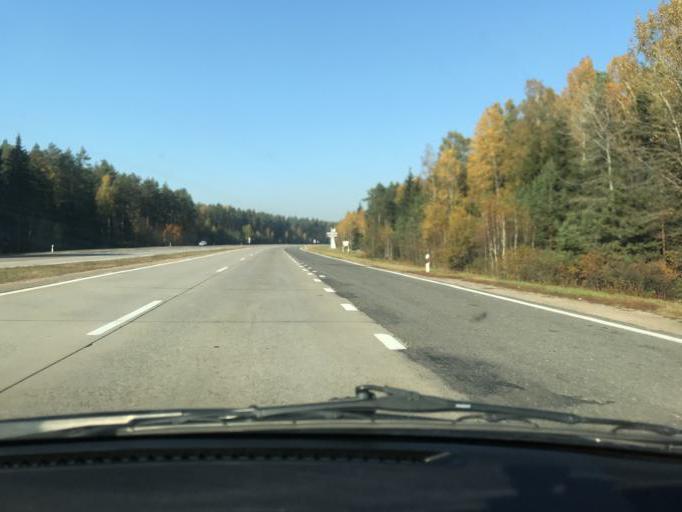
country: BY
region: Minsk
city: Uzda
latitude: 53.3784
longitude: 27.4946
